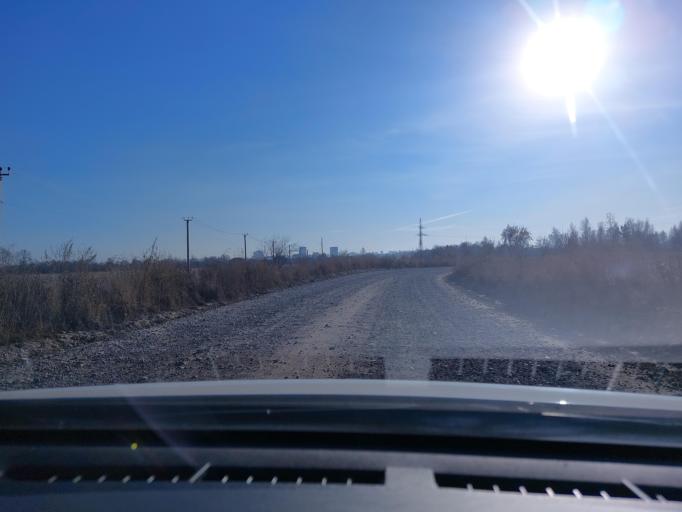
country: RU
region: Irkutsk
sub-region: Irkutskiy Rayon
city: Irkutsk
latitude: 52.3045
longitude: 104.2764
